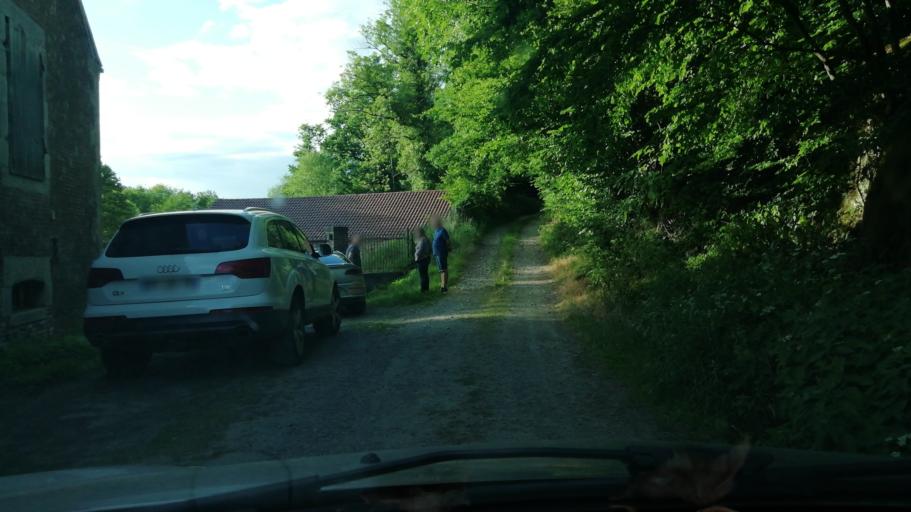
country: BE
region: Wallonia
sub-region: Province du Hainaut
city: Merbes-le-Chateau
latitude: 50.2691
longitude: 4.1839
